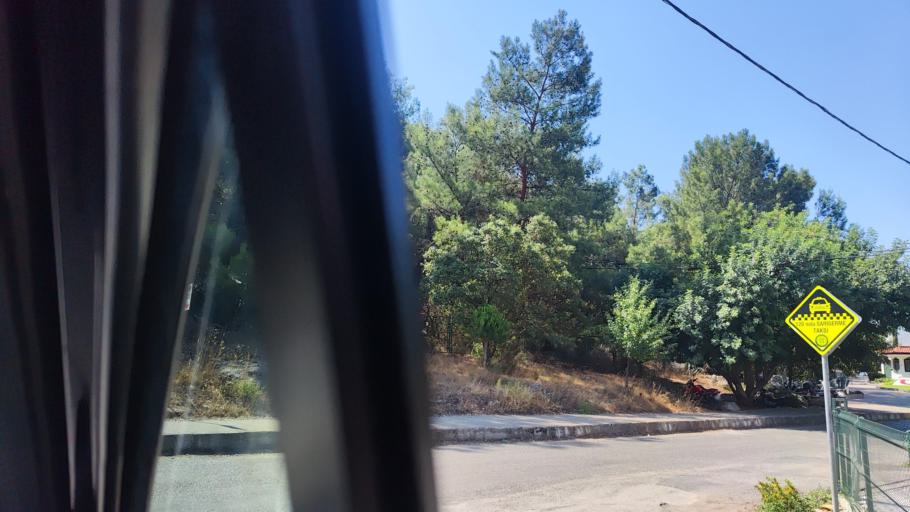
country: TR
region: Mugla
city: Sarigerme
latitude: 36.7081
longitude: 28.6987
